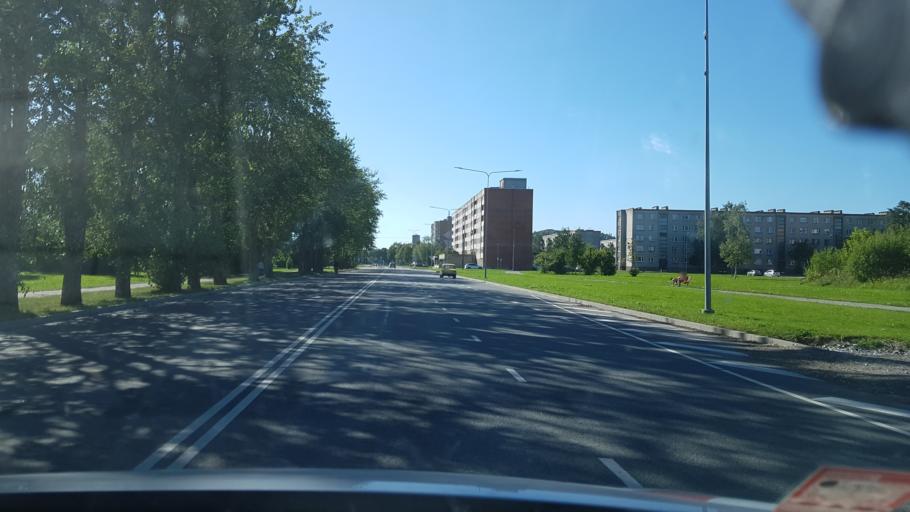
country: EE
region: Ida-Virumaa
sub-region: Kivioli linn
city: Kivioli
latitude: 59.3590
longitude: 26.9829
